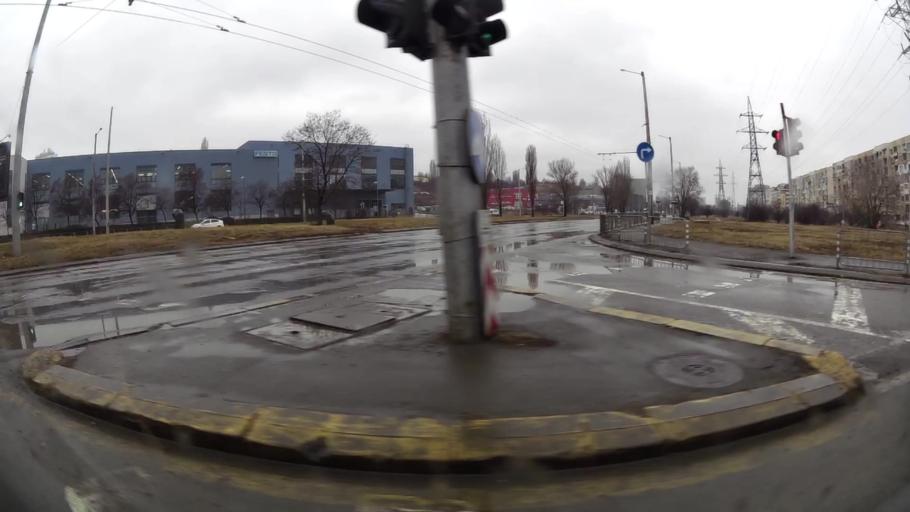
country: BG
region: Sofia-Capital
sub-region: Stolichna Obshtina
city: Sofia
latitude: 42.6636
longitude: 23.3900
